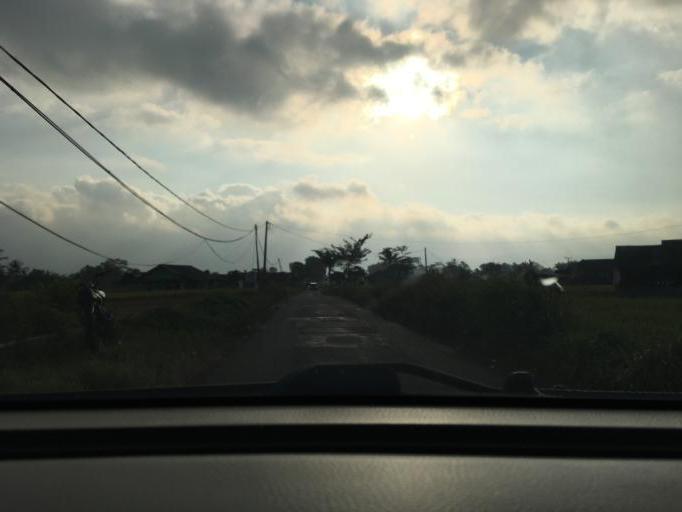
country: ID
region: West Java
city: Rawa
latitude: -7.0332
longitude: 108.3379
